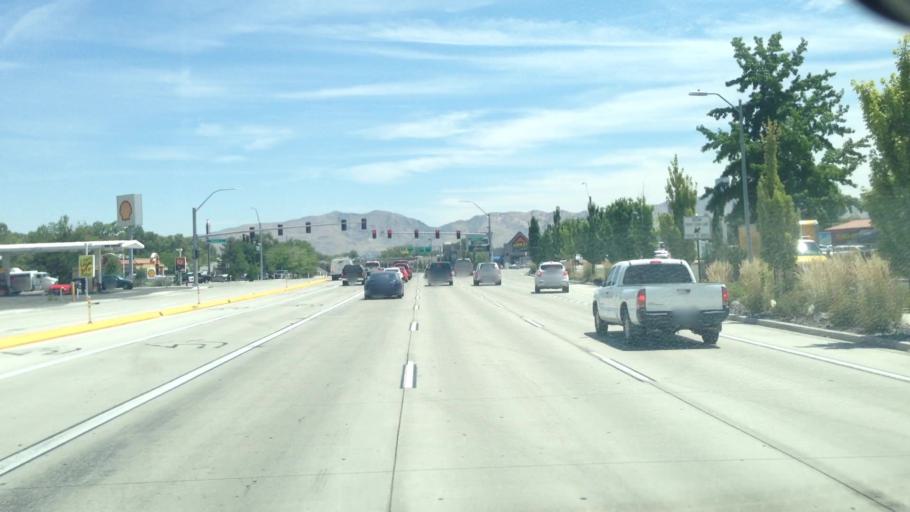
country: US
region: Nevada
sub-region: Washoe County
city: Reno
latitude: 39.4928
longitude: -119.7908
